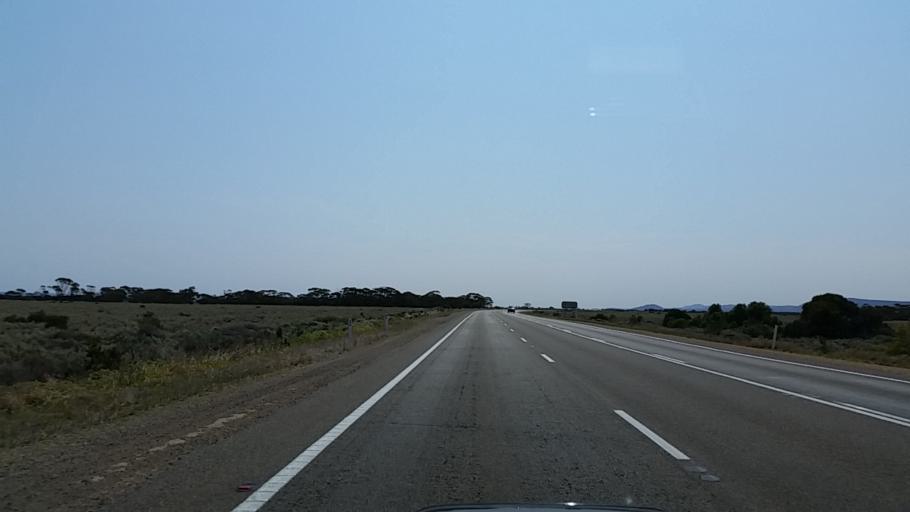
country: AU
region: South Australia
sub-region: Port Pirie City and Dists
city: Port Pirie
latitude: -32.9789
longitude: 137.9837
